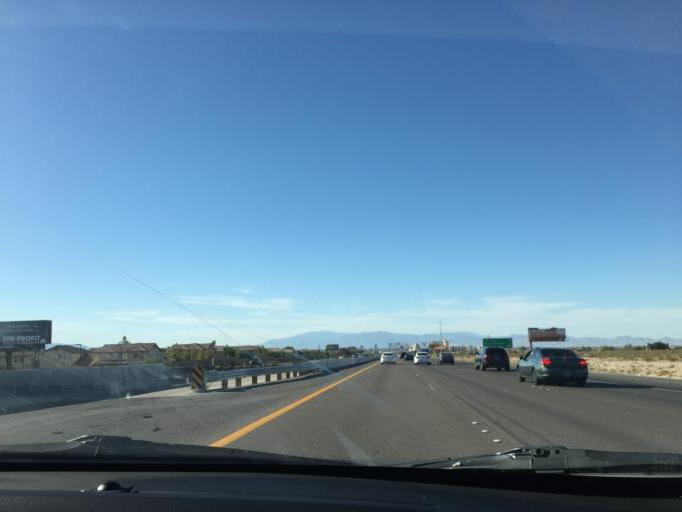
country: US
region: Nevada
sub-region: Clark County
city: Enterprise
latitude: 35.9727
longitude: -115.1813
